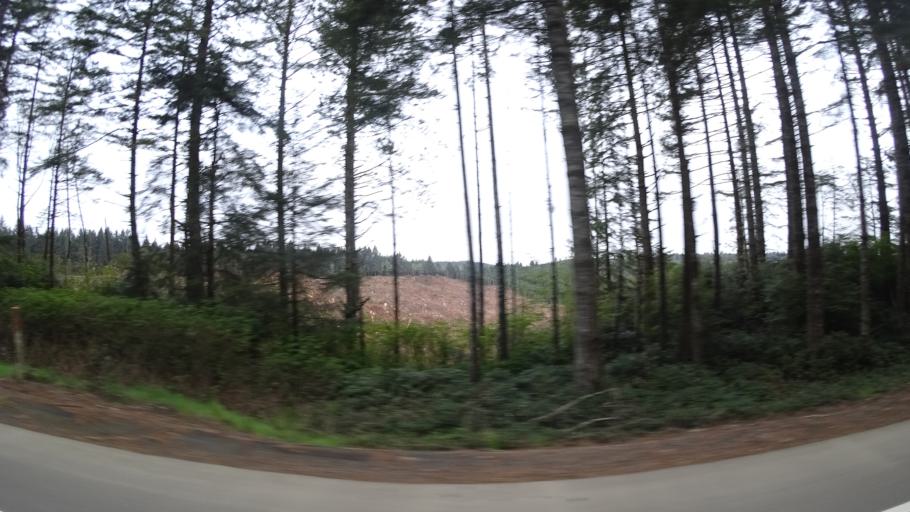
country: US
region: Oregon
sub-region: Coos County
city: Coquille
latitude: 43.2126
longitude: -124.3075
